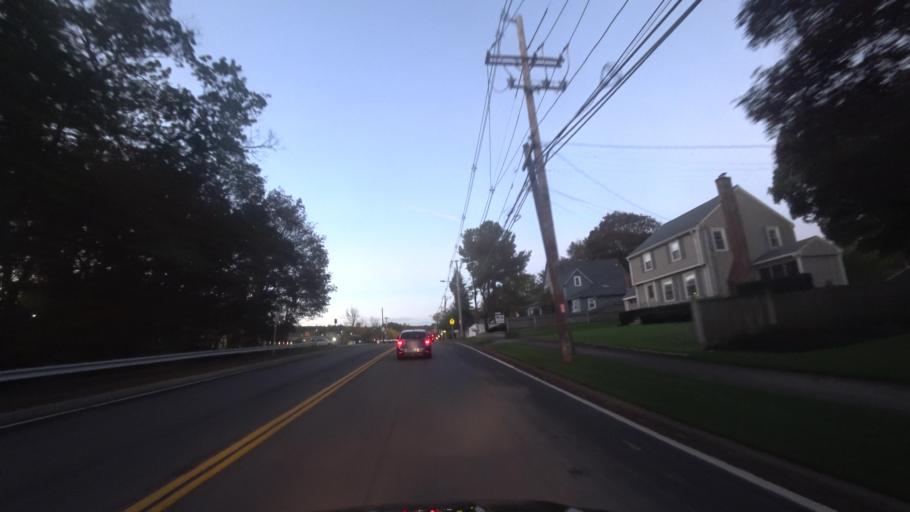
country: US
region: Massachusetts
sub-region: Middlesex County
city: Wakefield
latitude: 42.4994
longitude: -71.0509
